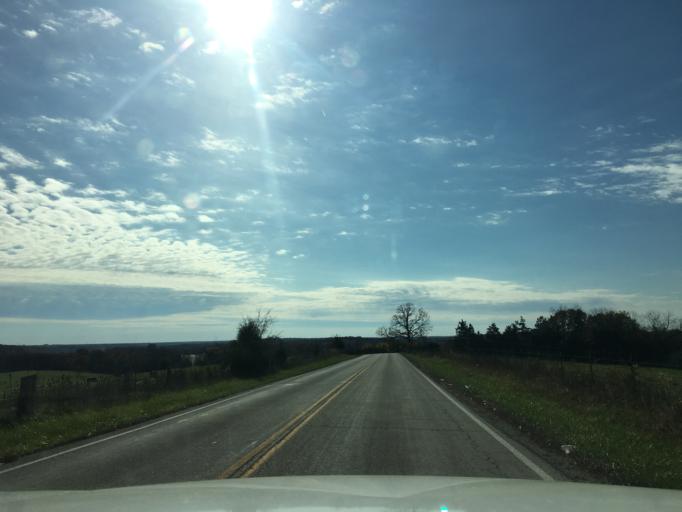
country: US
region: Missouri
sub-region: Osage County
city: Linn
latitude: 38.4102
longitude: -91.8156
